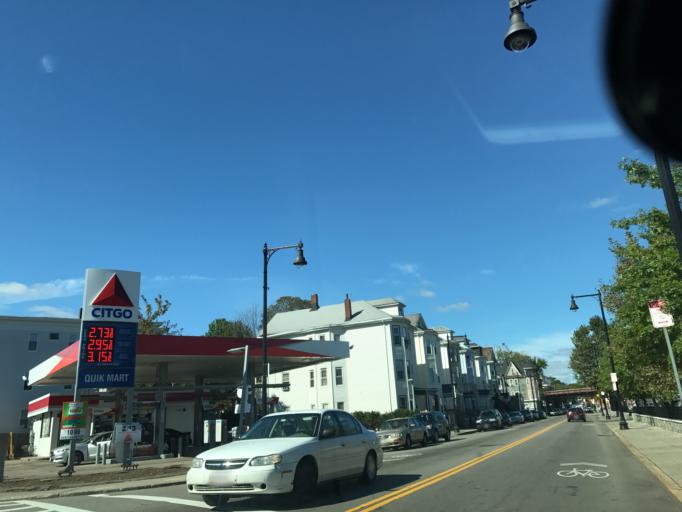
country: US
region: Massachusetts
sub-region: Suffolk County
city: South Boston
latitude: 42.2982
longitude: -71.0623
